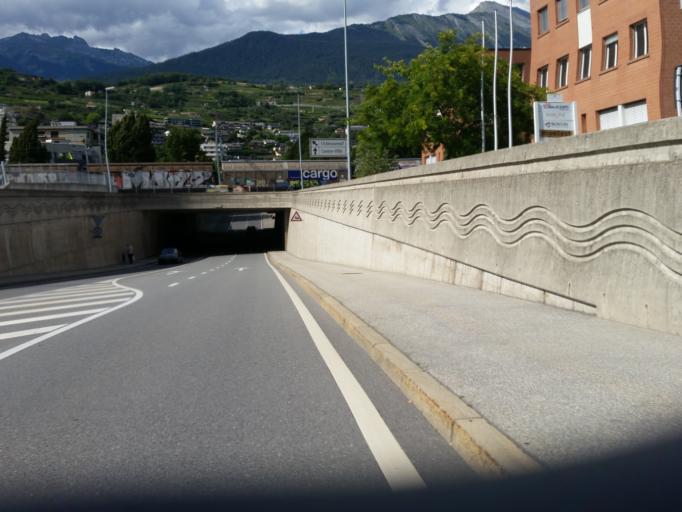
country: CH
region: Valais
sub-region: Sion District
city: Sitten
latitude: 46.2242
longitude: 7.3479
